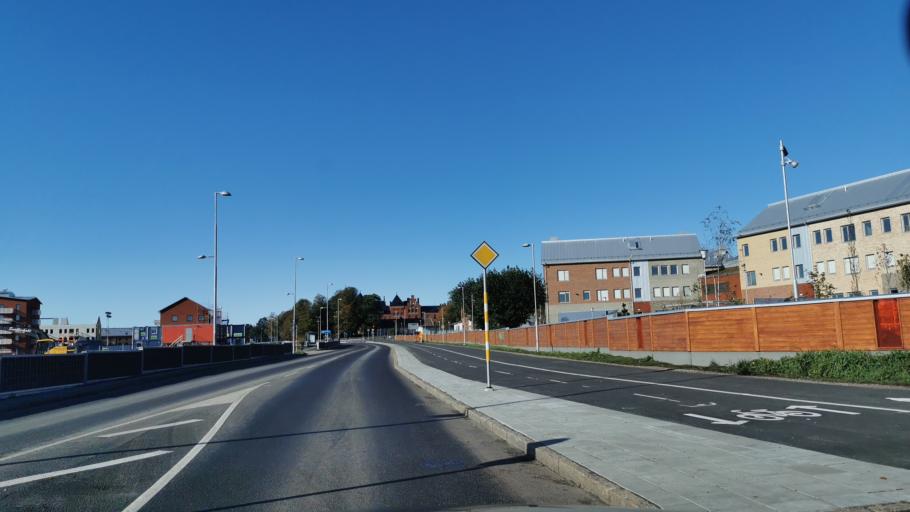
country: SE
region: Vaestra Goetaland
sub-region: Goteborg
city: Eriksbo
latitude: 57.7348
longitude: 12.0396
